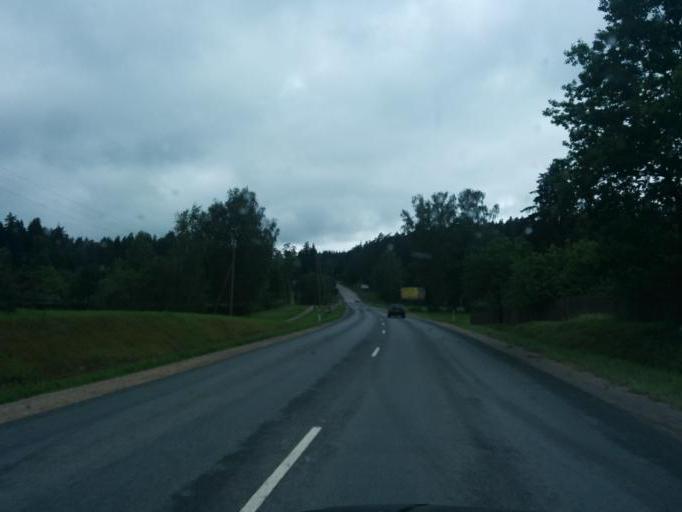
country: LV
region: Smiltene
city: Smiltene
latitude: 57.4163
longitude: 25.9309
